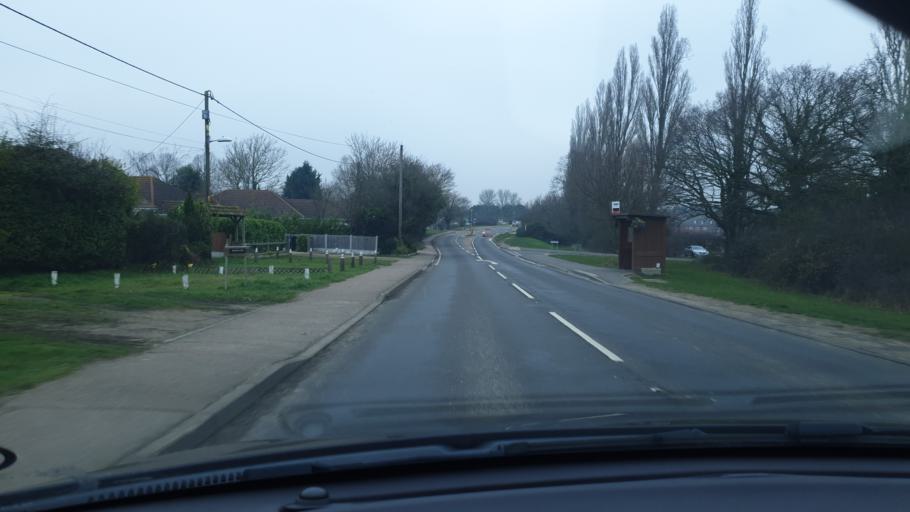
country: GB
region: England
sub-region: Essex
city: Little Clacton
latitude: 51.8500
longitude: 1.1183
